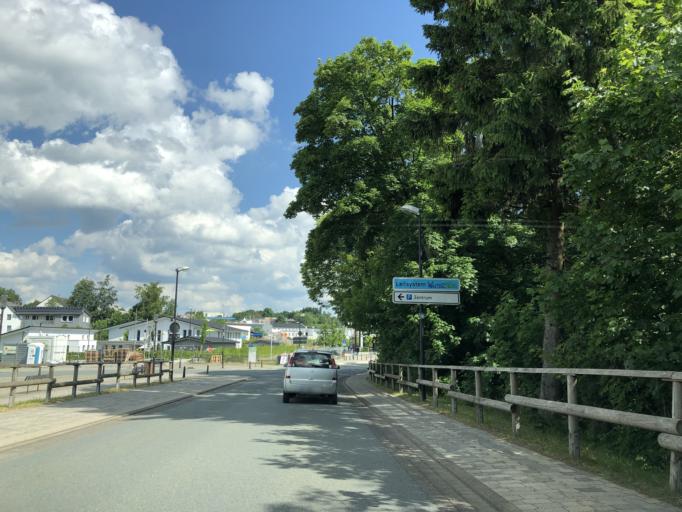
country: DE
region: North Rhine-Westphalia
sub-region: Regierungsbezirk Arnsberg
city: Winterberg
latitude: 51.1968
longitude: 8.5326
